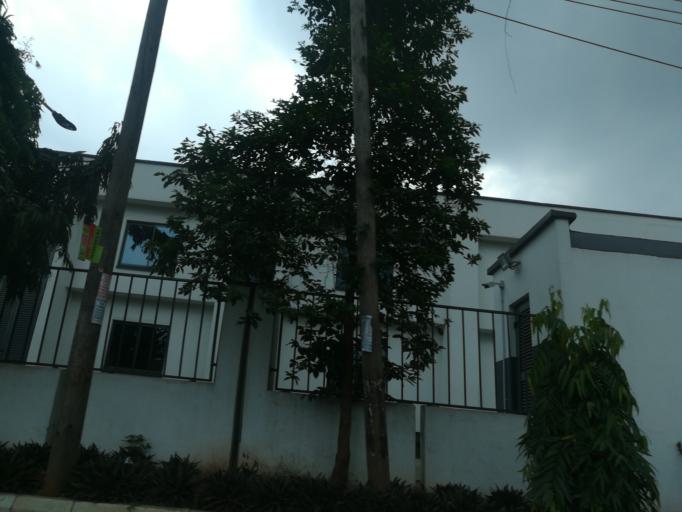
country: NG
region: Lagos
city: Ojota
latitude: 6.5960
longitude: 3.3694
